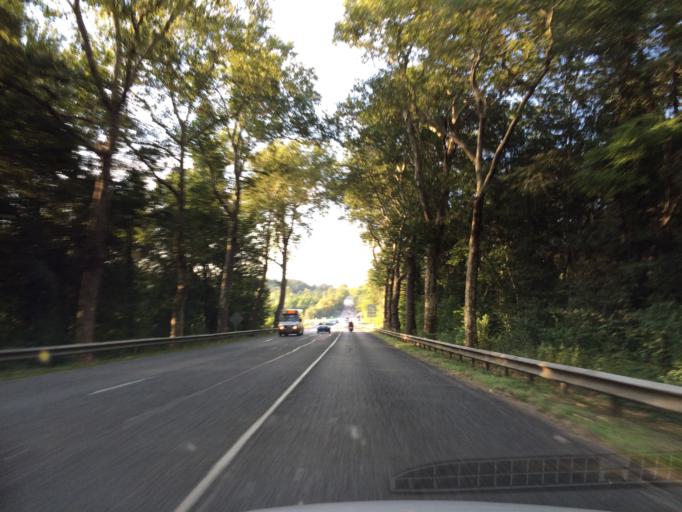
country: FR
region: Bourgogne
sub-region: Departement de l'Yonne
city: Moneteau
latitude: 47.8332
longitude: 3.5531
